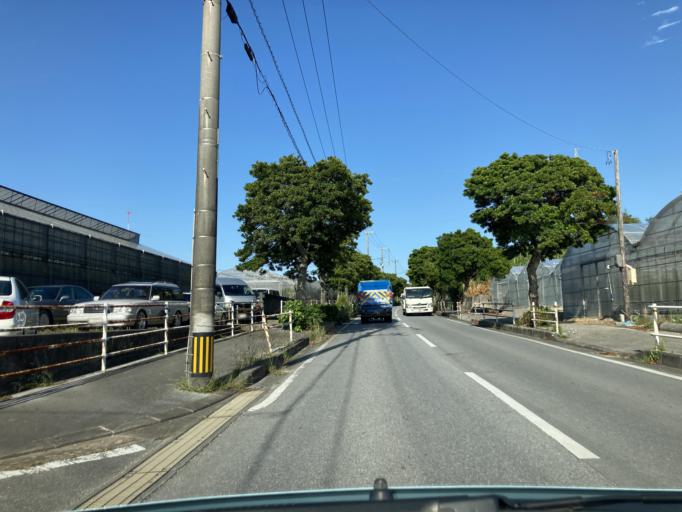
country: JP
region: Okinawa
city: Tomigusuku
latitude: 26.1719
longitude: 127.7034
